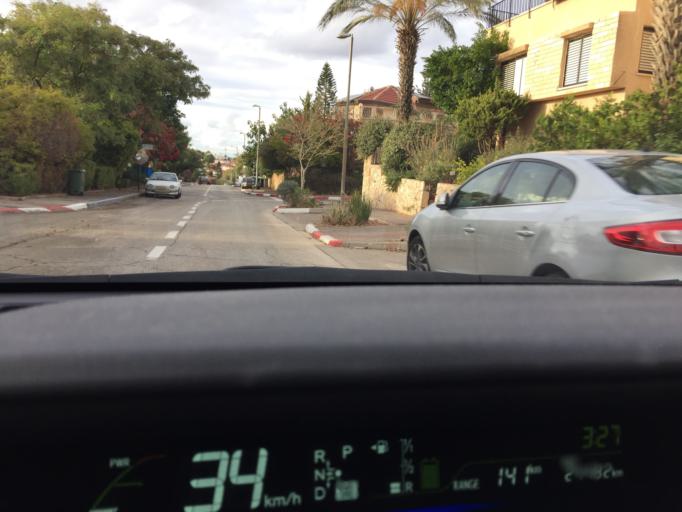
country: PS
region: West Bank
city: Az Zawiyah
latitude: 32.1097
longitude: 35.0317
